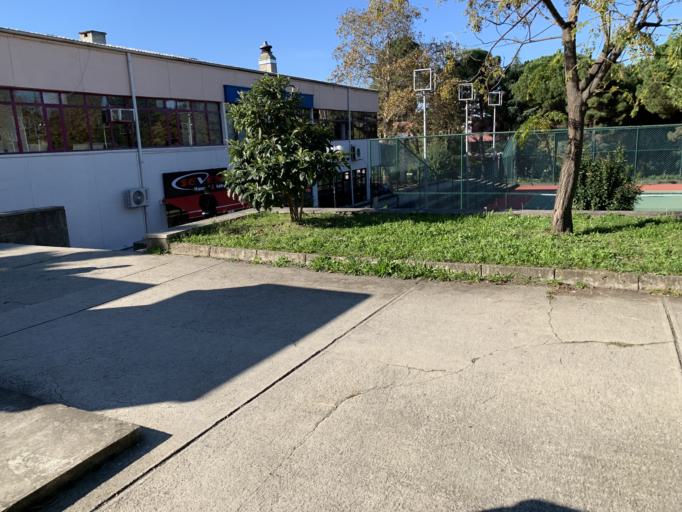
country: TR
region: Trabzon
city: Trabzon
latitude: 40.9964
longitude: 39.7685
